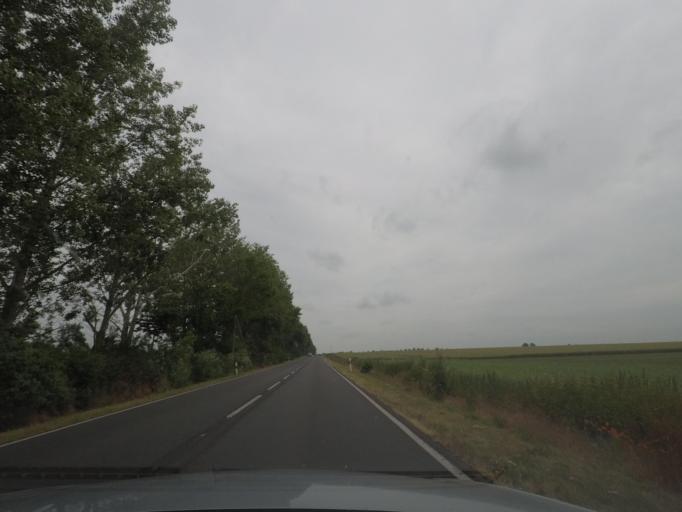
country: DE
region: Saxony-Anhalt
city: Wanzleben
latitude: 52.0461
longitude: 11.4172
